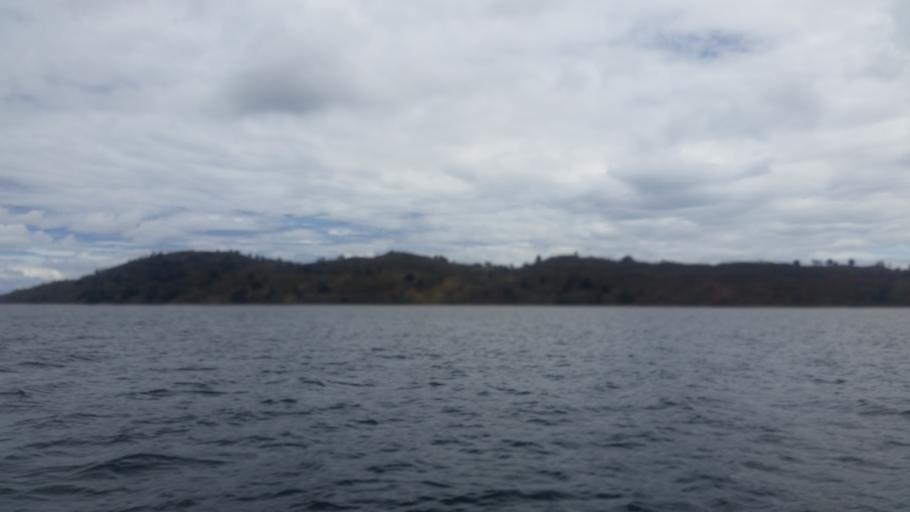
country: PE
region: Puno
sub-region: Provincia de Puno
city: Taquile
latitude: -15.7923
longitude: -69.6972
